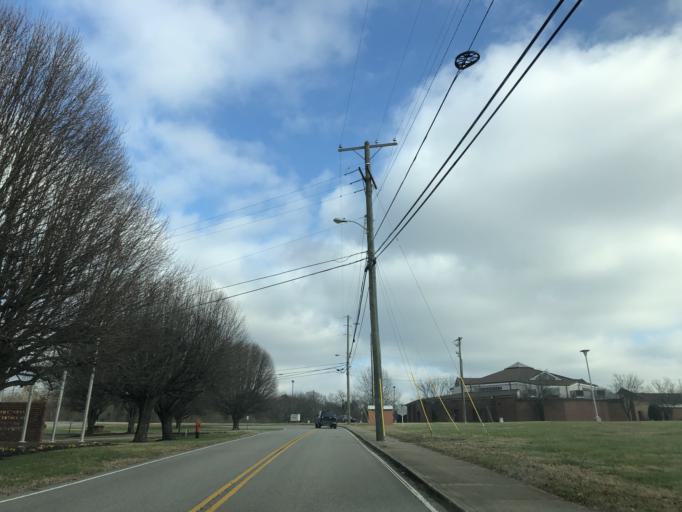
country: US
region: Tennessee
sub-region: Davidson County
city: Nashville
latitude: 36.2045
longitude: -86.7965
